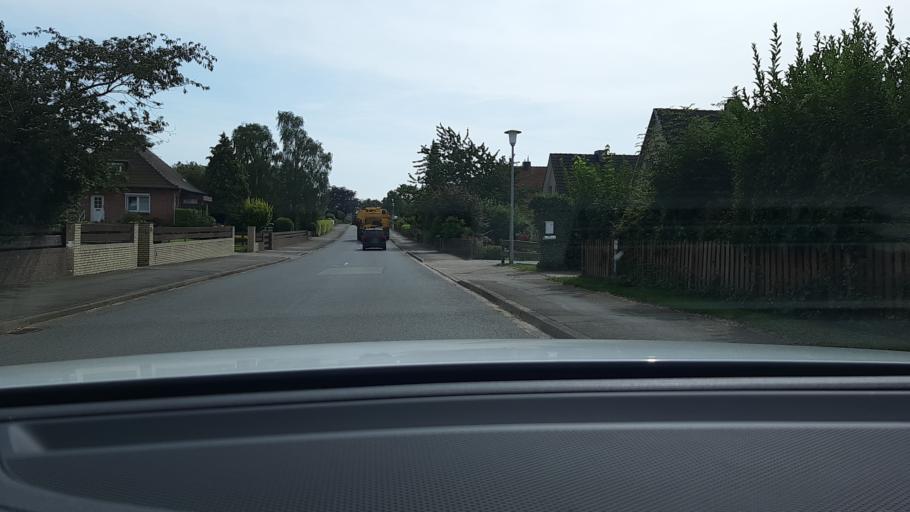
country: DE
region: Schleswig-Holstein
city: Rehhorst
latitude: 53.8718
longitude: 10.4716
